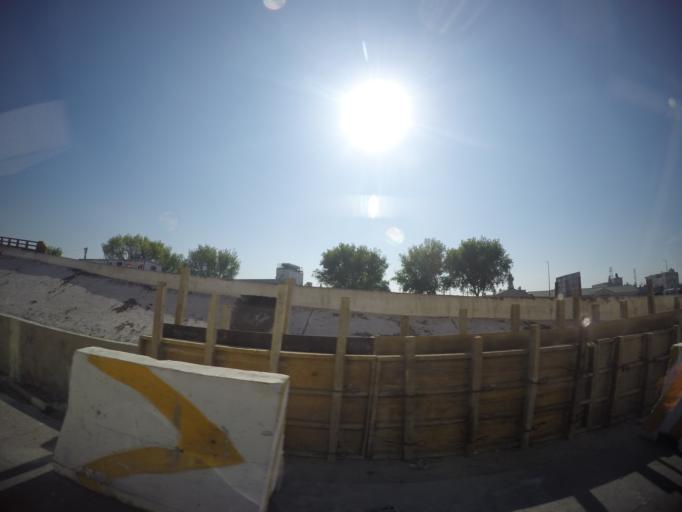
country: MX
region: Mexico
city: Santo Tomas Chiconautla
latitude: 19.6123
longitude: -99.0085
